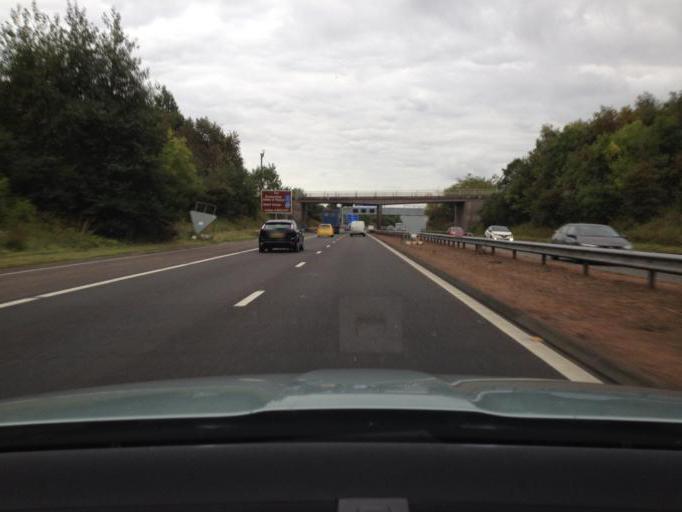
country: GB
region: Scotland
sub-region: Fife
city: Crossgates
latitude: 56.0571
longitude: -3.3873
